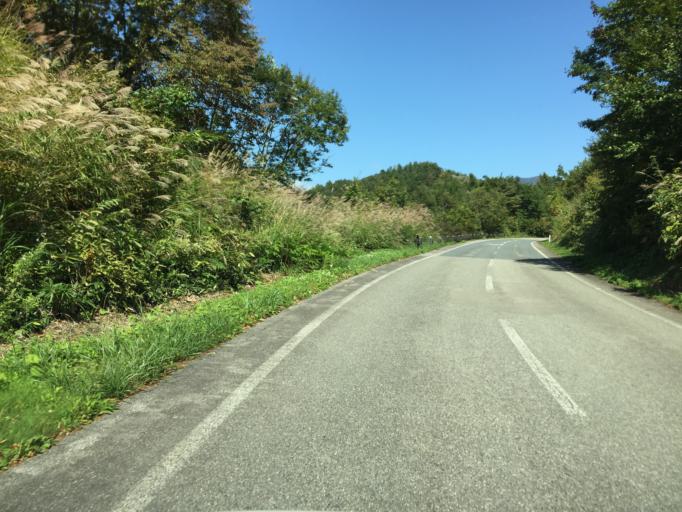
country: JP
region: Fukushima
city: Inawashiro
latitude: 37.6741
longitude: 140.1196
